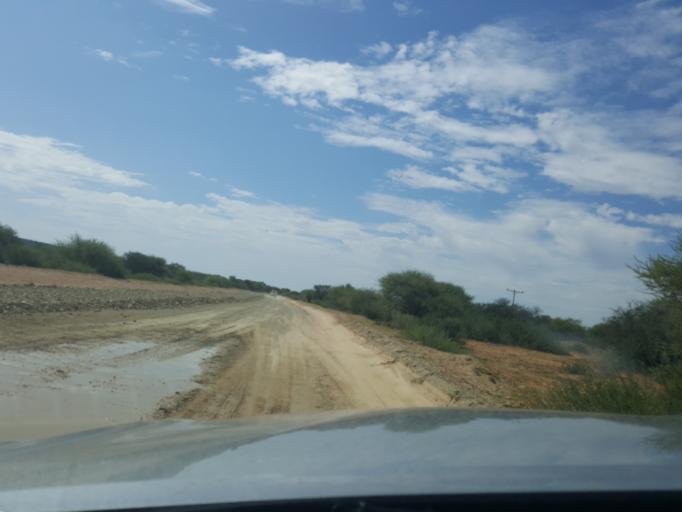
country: BW
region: Kweneng
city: Letlhakeng
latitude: -23.9827
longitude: 24.9676
